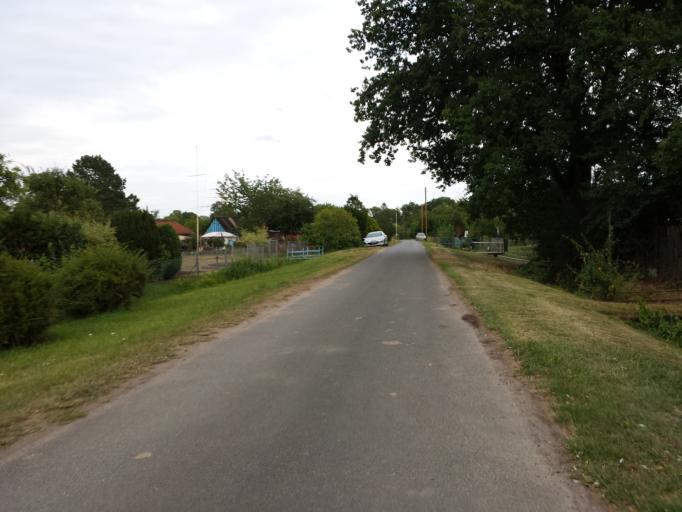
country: DE
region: Lower Saxony
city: Stuhr
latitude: 53.0690
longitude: 8.7539
